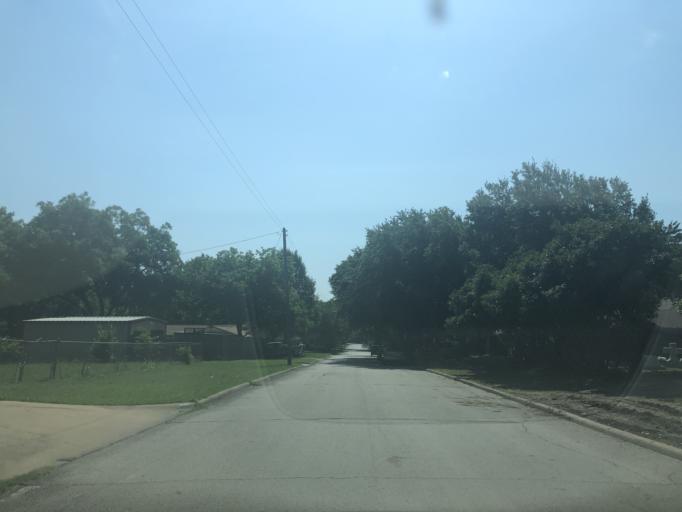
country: US
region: Texas
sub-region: Dallas County
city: Grand Prairie
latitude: 32.7319
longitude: -97.0037
